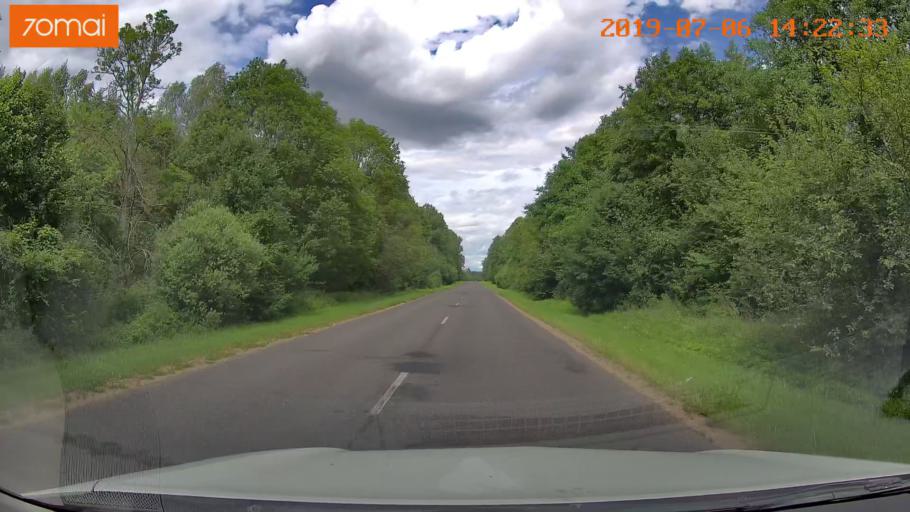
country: BY
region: Minsk
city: Ivyanyets
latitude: 53.9098
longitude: 26.7640
